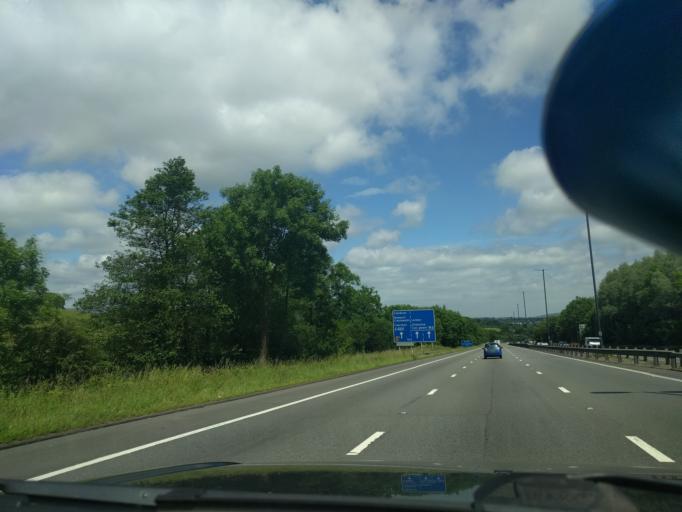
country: GB
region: Wales
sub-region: Newport
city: Newport
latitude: 51.5874
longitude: -3.0332
